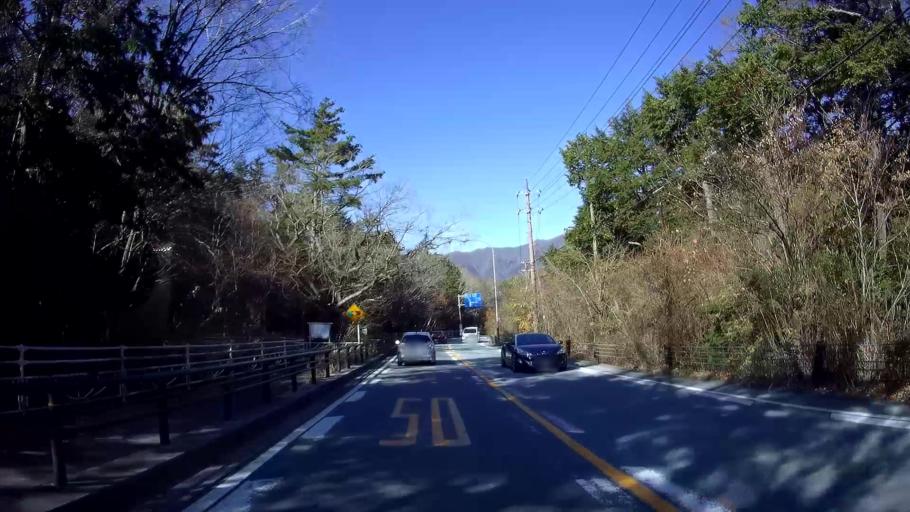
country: JP
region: Yamanashi
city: Fujikawaguchiko
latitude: 35.4776
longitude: 138.6613
